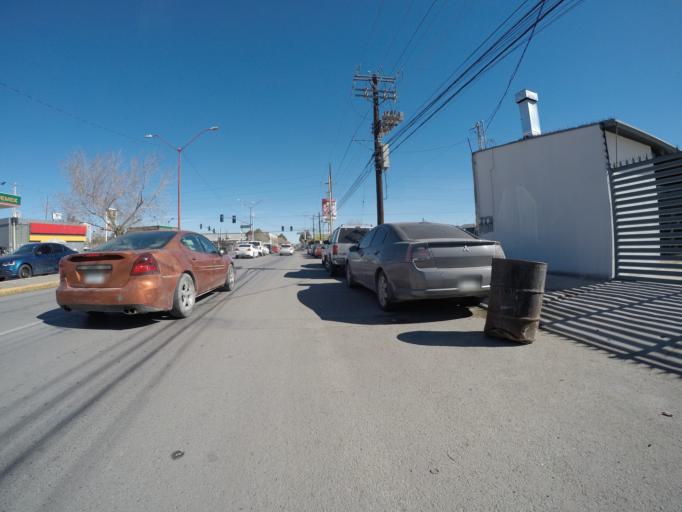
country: MX
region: Chihuahua
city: Ciudad Juarez
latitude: 31.7412
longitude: -106.4417
